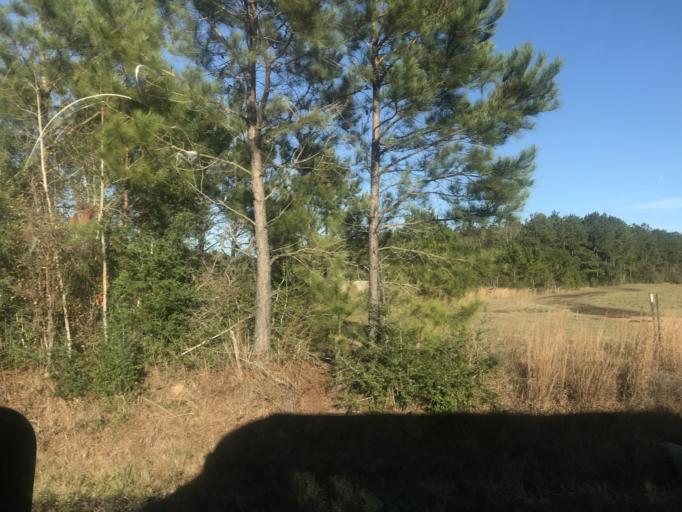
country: US
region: Louisiana
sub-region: Saint Tammany Parish
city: Covington
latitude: 30.5941
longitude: -90.1751
